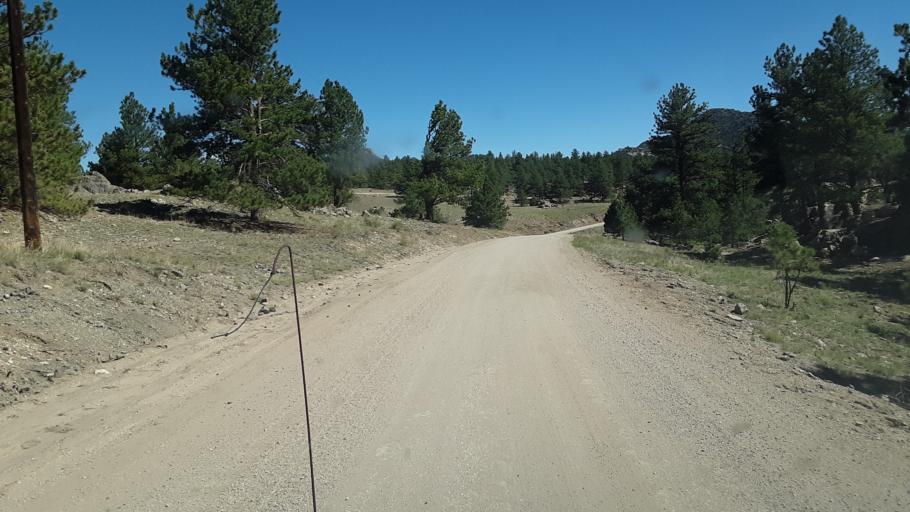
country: US
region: Colorado
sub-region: Custer County
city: Westcliffe
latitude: 38.2096
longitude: -105.4436
